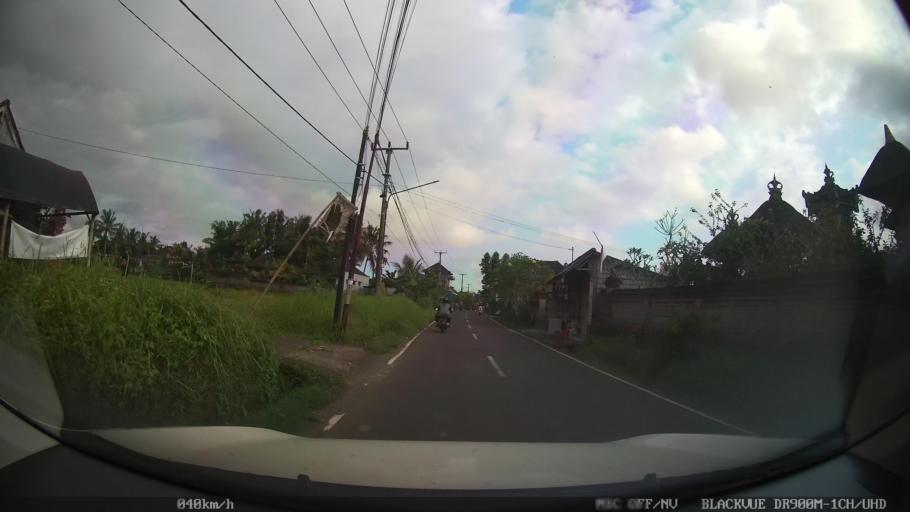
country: ID
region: Bali
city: Banjar Tebongkang
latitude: -8.5256
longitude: 115.2486
